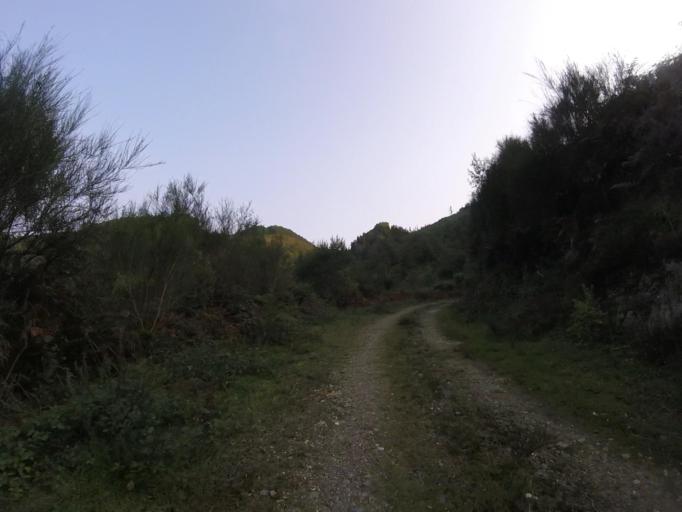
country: ES
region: Navarre
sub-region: Provincia de Navarra
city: Arano
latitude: 43.2534
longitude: -1.8438
